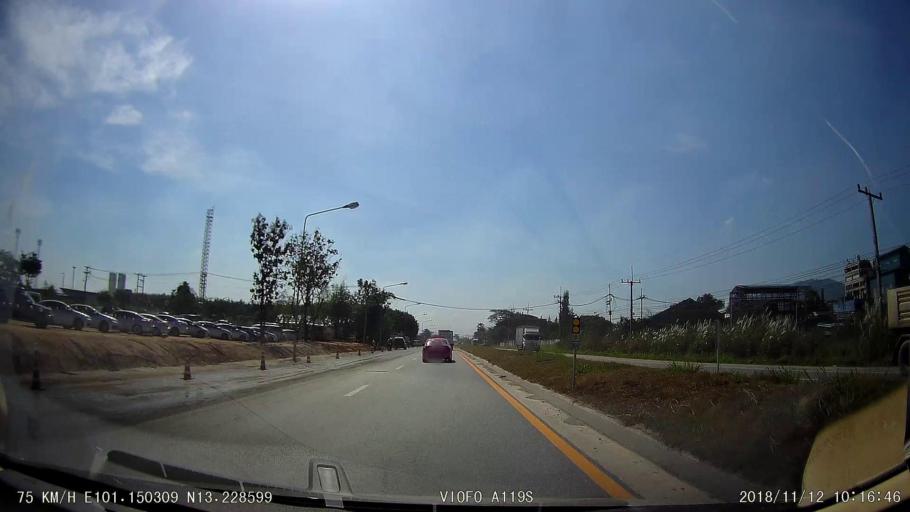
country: TH
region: Chon Buri
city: Ban Bueng
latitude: 13.2282
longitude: 101.1504
